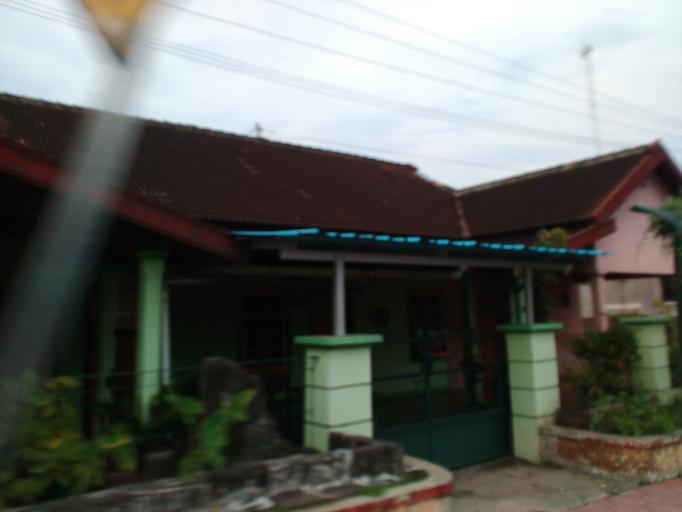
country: ID
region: Central Java
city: Boyolali
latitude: -7.5315
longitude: 110.5949
